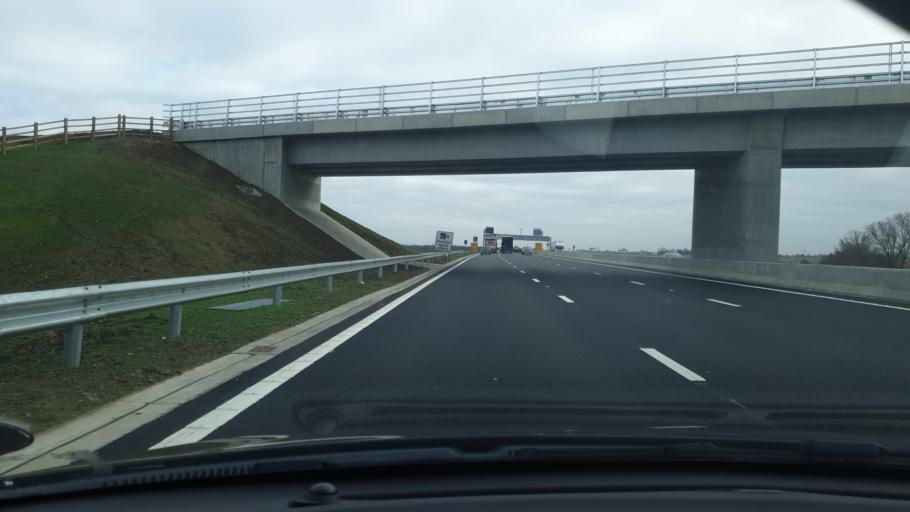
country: GB
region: England
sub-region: Cambridgeshire
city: Swavesey
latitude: 52.2860
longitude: -0.0486
